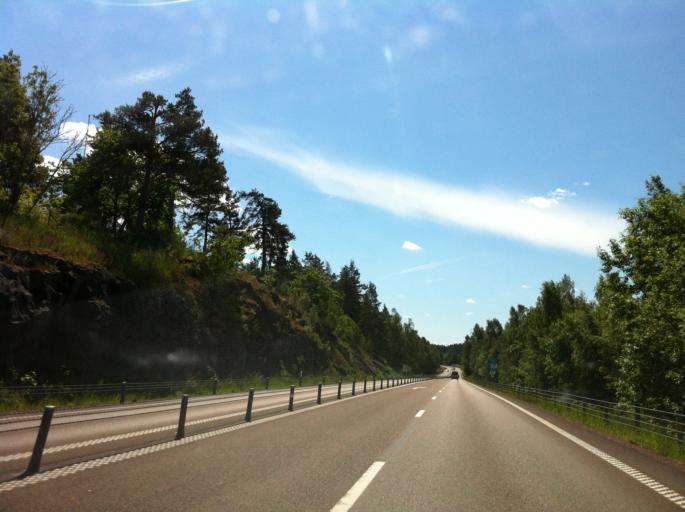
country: SE
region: Vaestra Goetaland
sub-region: Melleruds Kommun
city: Mellerud
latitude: 58.8203
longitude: 12.5232
